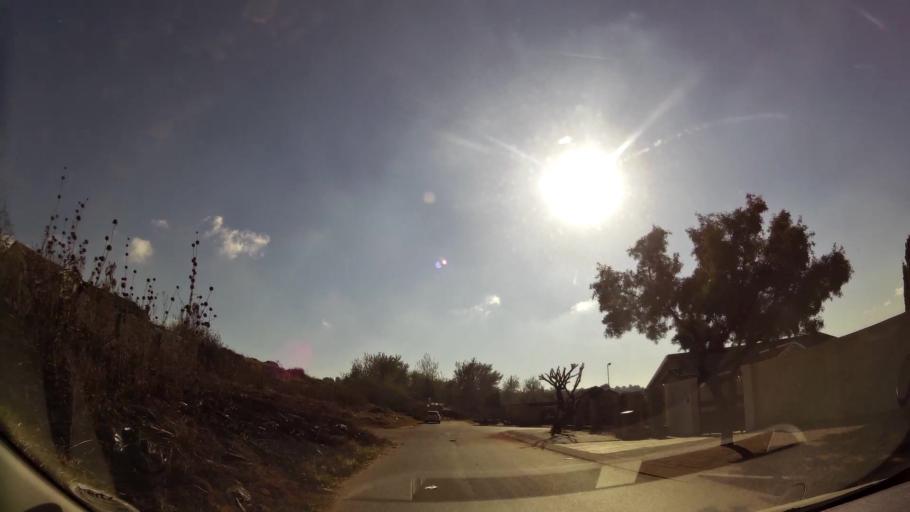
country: ZA
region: Gauteng
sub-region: City of Johannesburg Metropolitan Municipality
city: Roodepoort
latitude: -26.1557
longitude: 27.8360
